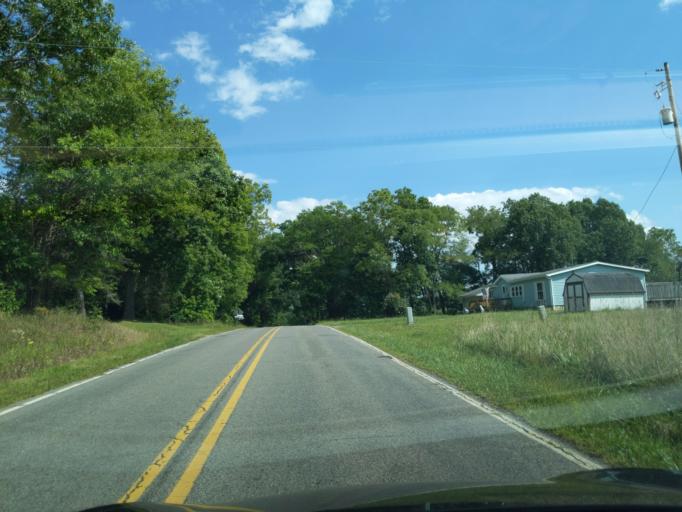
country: US
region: Michigan
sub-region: Jackson County
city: Jackson
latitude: 42.2979
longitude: -84.4962
